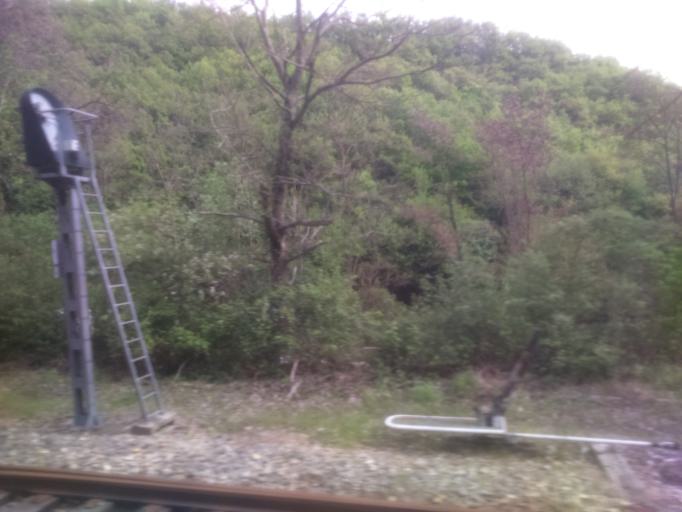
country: FR
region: Rhone-Alpes
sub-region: Departement de l'Isere
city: Saint-Georges-de-Commiers
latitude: 45.0454
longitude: 5.6908
